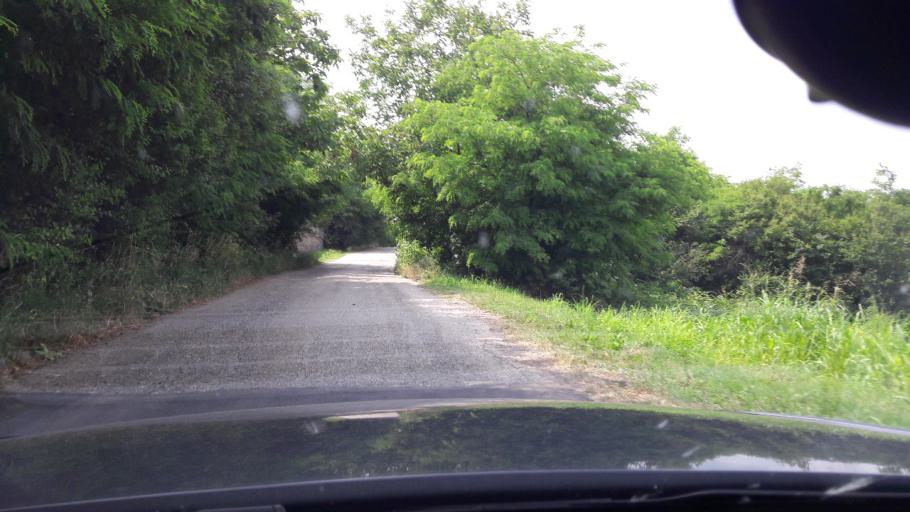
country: RS
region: Central Serbia
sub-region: Belgrade
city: Sopot
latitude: 44.6092
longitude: 20.5980
